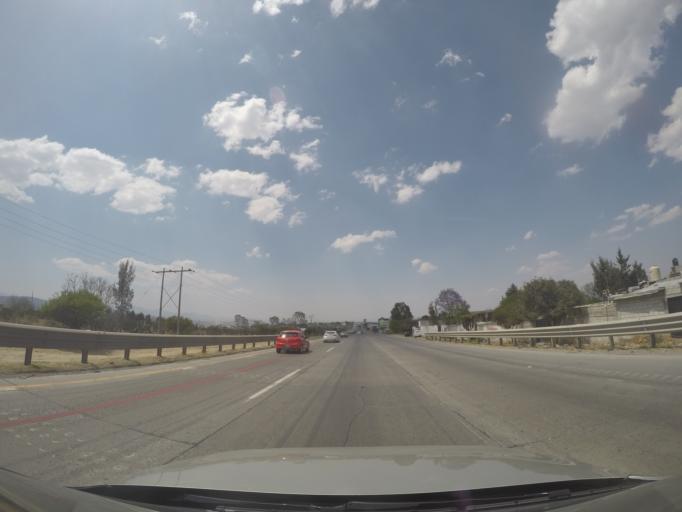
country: MX
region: Queretaro
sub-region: San Juan del Rio
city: Paso de Mata
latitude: 20.3473
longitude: -99.9494
